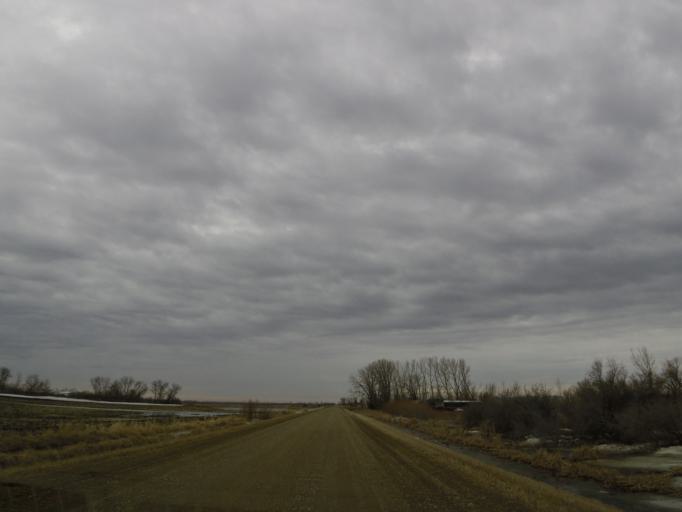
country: US
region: North Dakota
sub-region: Walsh County
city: Grafton
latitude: 48.4185
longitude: -97.4484
